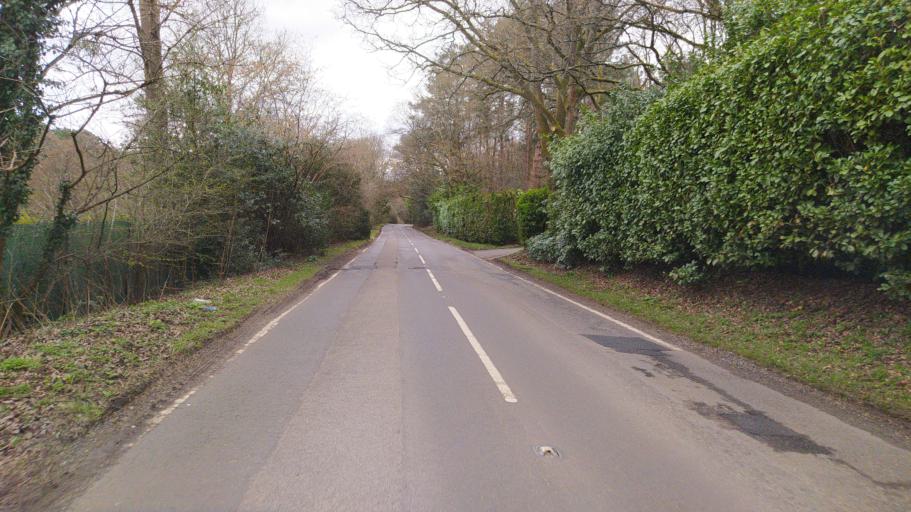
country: GB
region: England
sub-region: Surrey
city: Churt
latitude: 51.1727
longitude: -0.7490
